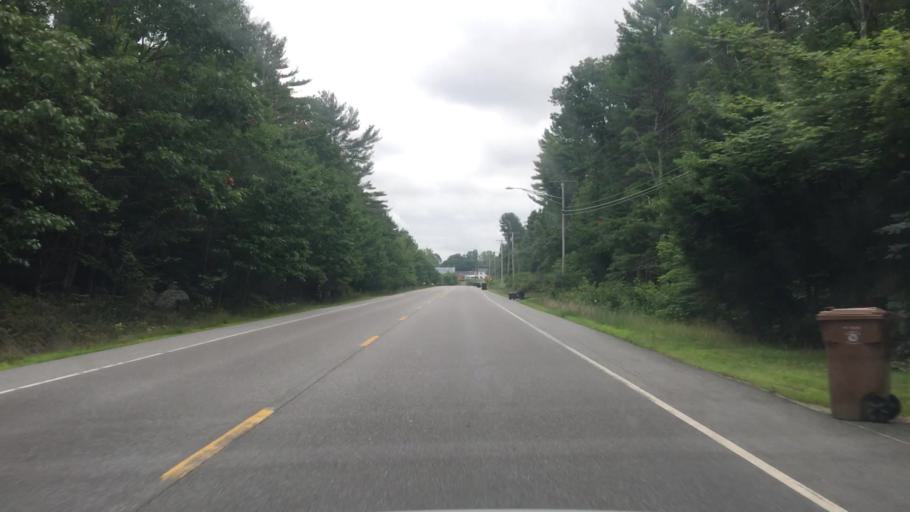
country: US
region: Maine
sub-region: York County
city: Biddeford
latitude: 43.5251
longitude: -70.4946
